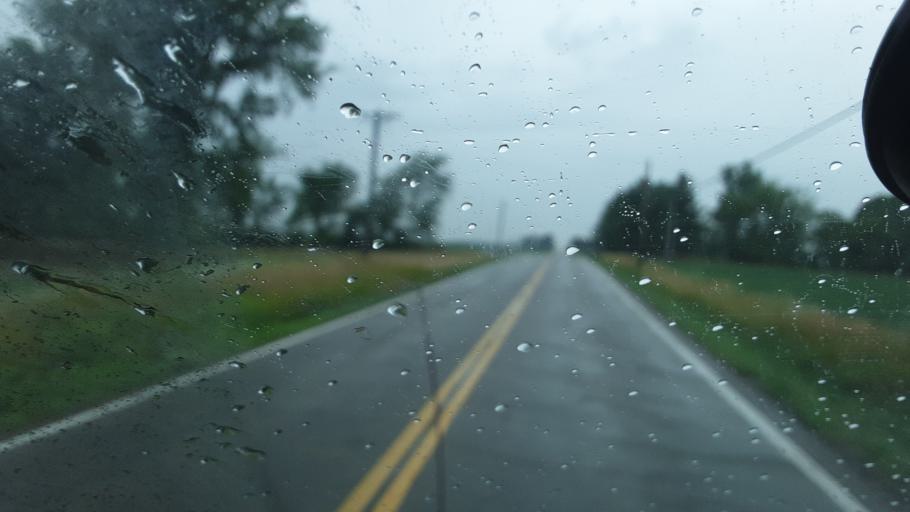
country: US
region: Ohio
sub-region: Williams County
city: Montpelier
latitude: 41.5346
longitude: -84.6130
